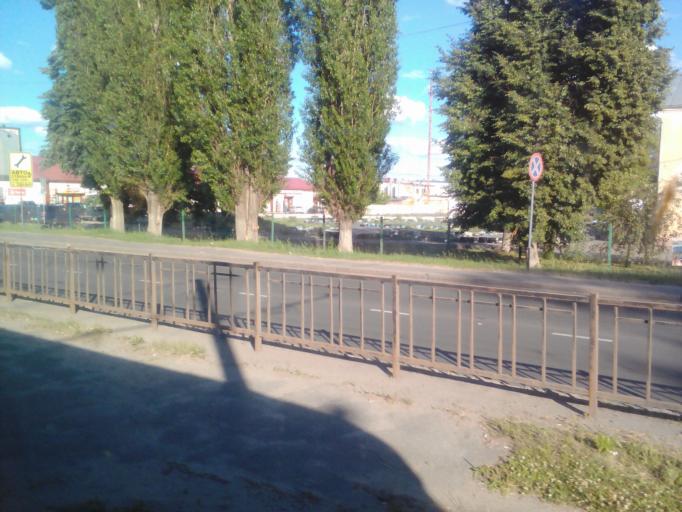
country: RU
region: Kursk
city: Kursk
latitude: 51.7056
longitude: 36.1729
